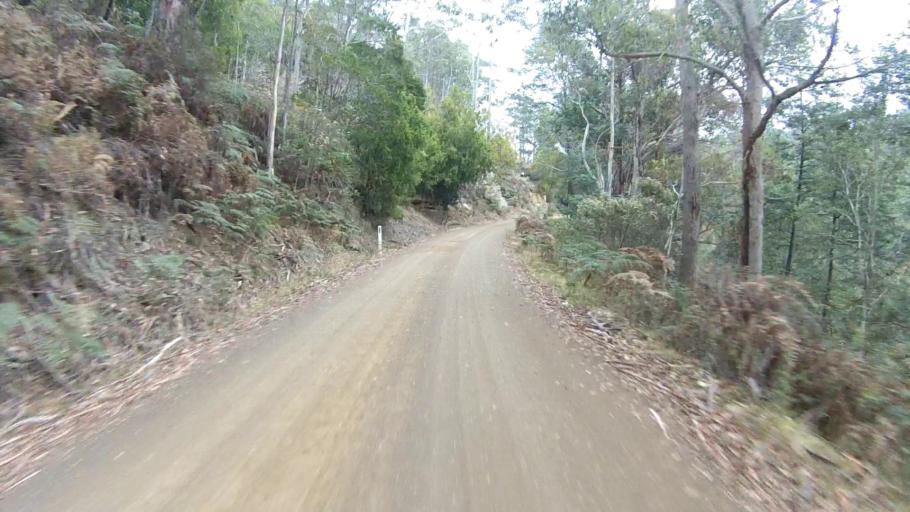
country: AU
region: Tasmania
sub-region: Huon Valley
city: Cygnet
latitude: -43.2272
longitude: 147.1657
